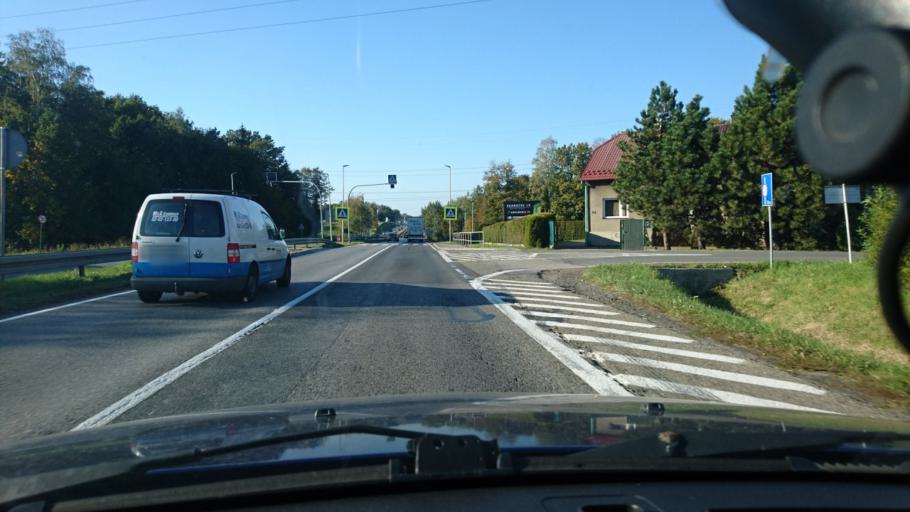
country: PL
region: Silesian Voivodeship
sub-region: Powiat bielski
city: Mazancowice
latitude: 49.8637
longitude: 19.0144
